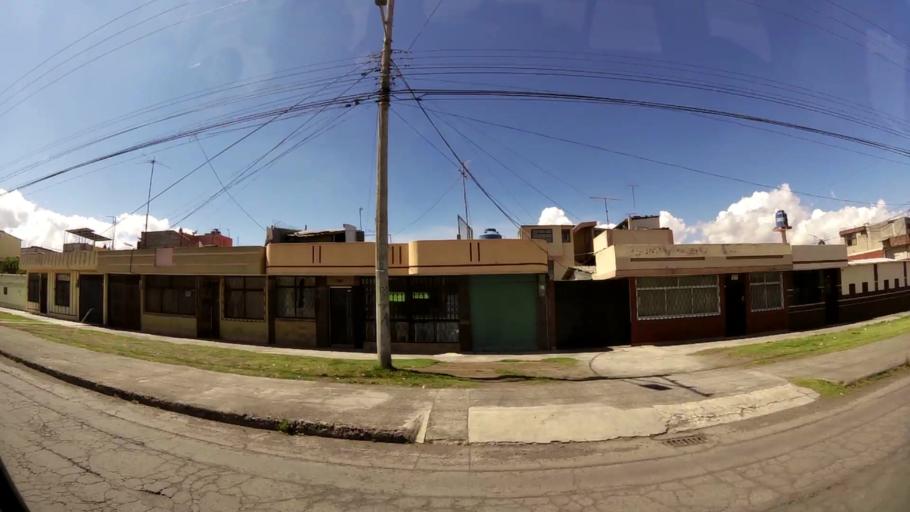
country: EC
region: Chimborazo
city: Riobamba
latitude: -1.6798
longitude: -78.6344
